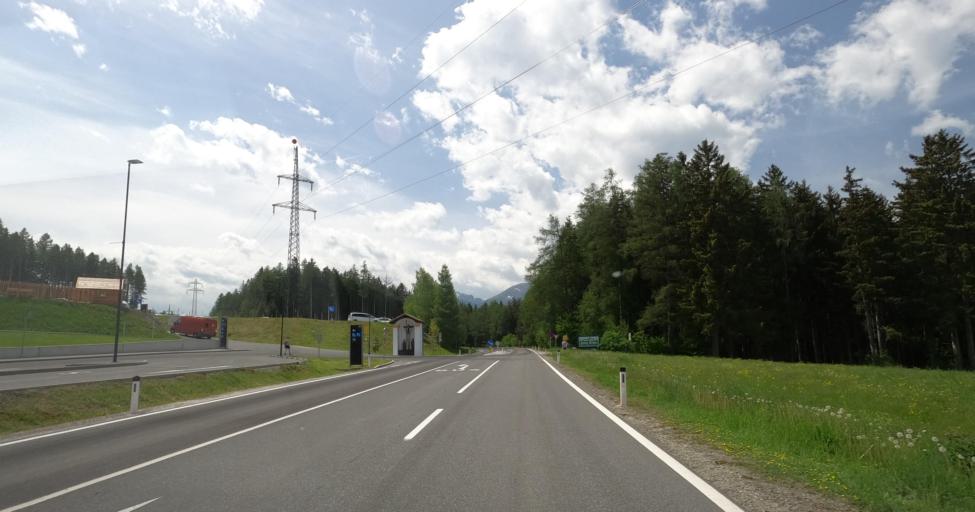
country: AT
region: Tyrol
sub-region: Politischer Bezirk Innsbruck Land
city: Patsch
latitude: 47.2222
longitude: 11.4254
